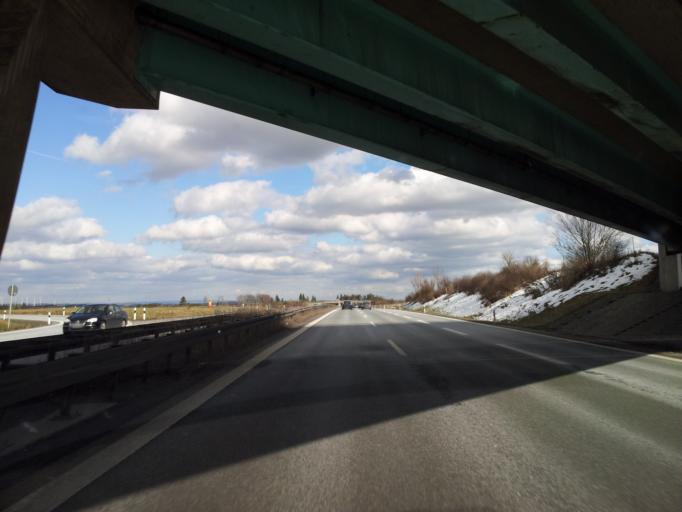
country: DE
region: Bavaria
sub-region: Upper Franconia
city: Koditz
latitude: 50.3429
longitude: 11.8311
